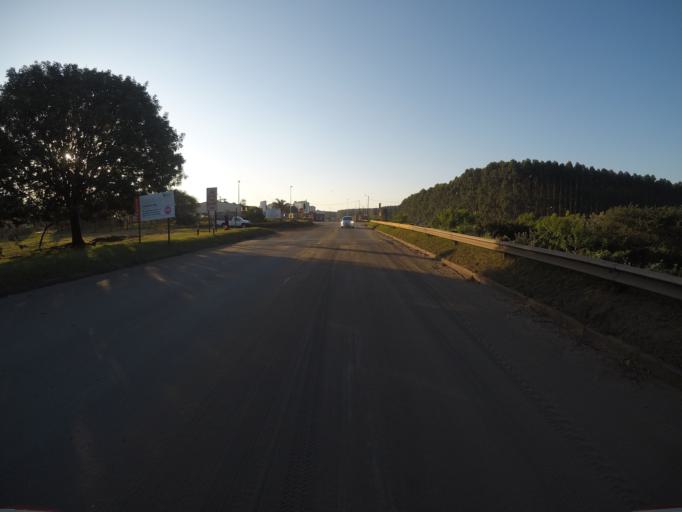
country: ZA
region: KwaZulu-Natal
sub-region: uThungulu District Municipality
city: KwaMbonambi
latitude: -28.6840
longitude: 32.1422
